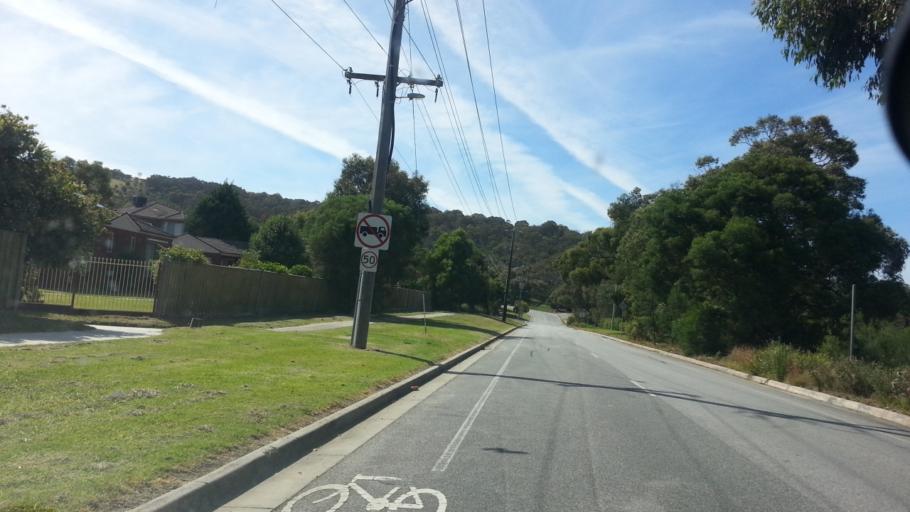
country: AU
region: Victoria
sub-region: Knox
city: Rowville
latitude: -37.9419
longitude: 145.2453
